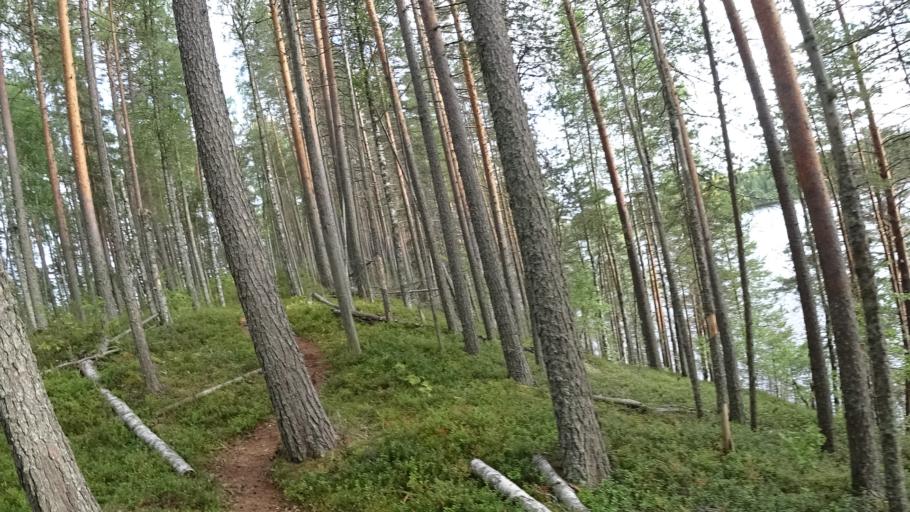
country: FI
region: North Karelia
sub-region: Joensuu
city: Ilomantsi
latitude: 62.5725
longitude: 31.1752
